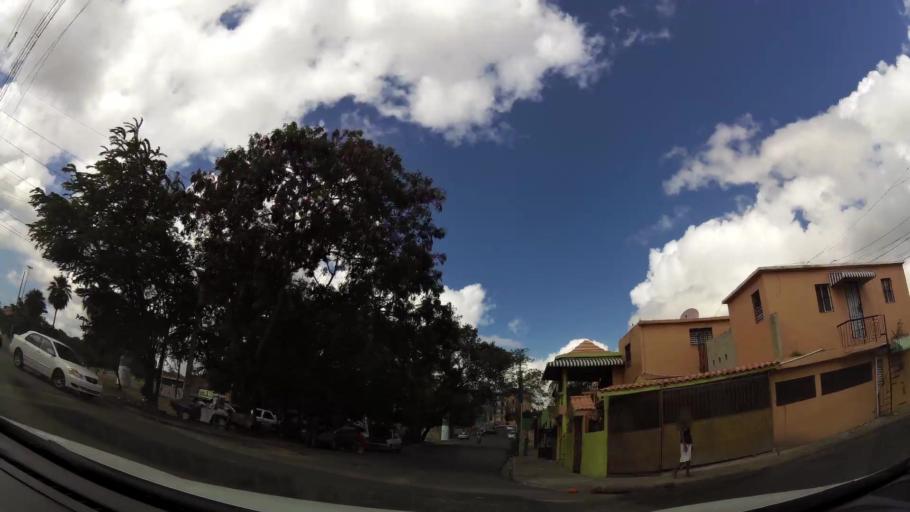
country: DO
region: Nacional
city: San Carlos
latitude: 18.4885
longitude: -69.8844
